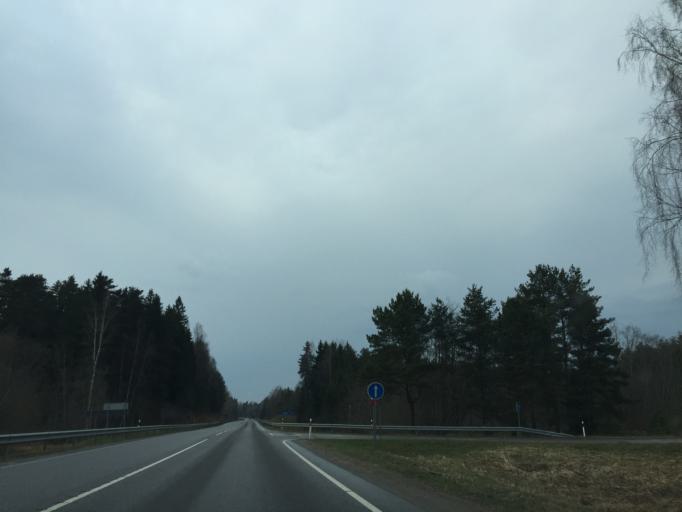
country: EE
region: Tartu
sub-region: UElenurme vald
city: Ulenurme
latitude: 58.1152
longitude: 26.7349
